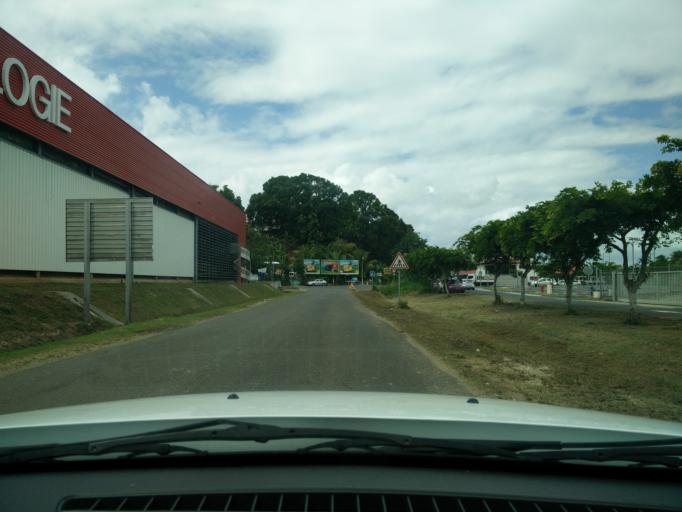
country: GP
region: Guadeloupe
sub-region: Guadeloupe
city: Petit-Bourg
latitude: 16.2038
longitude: -61.6067
